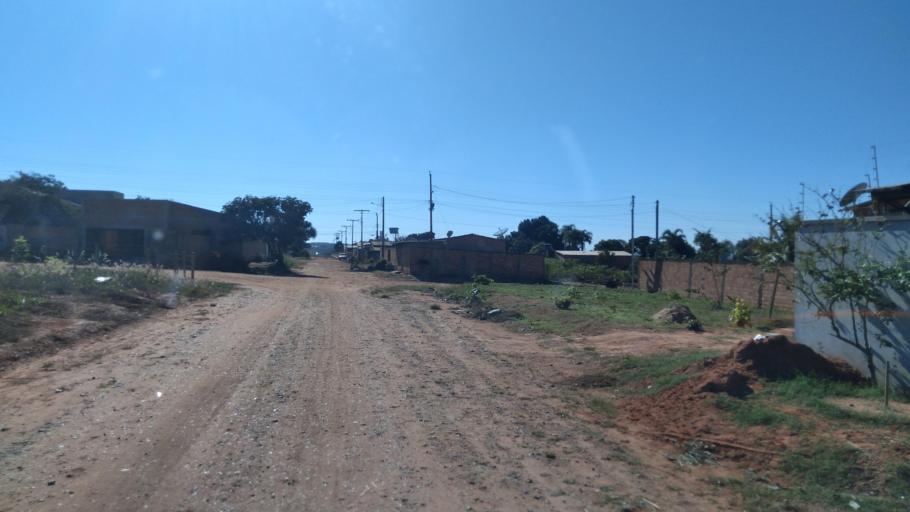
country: BR
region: Goias
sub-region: Mineiros
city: Mineiros
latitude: -17.5934
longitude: -52.5555
